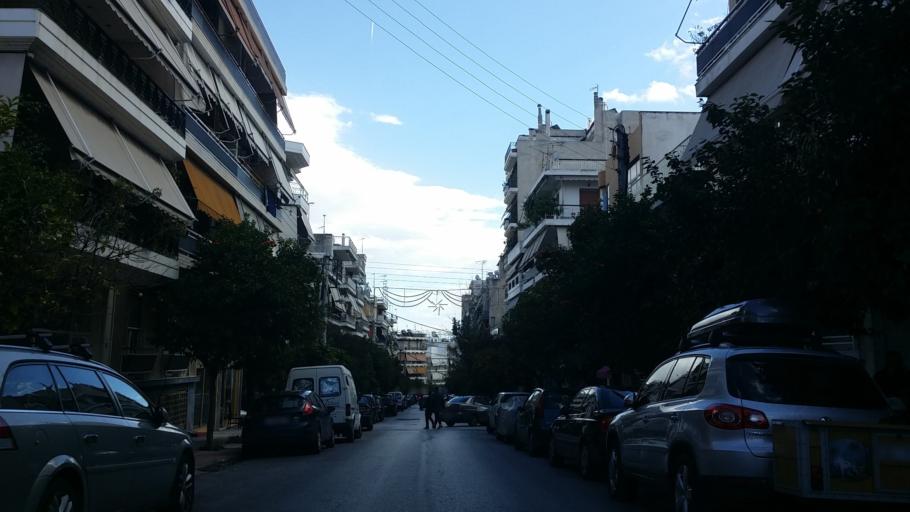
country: GR
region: Attica
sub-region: Nomos Piraios
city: Korydallos
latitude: 37.9798
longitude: 23.6472
